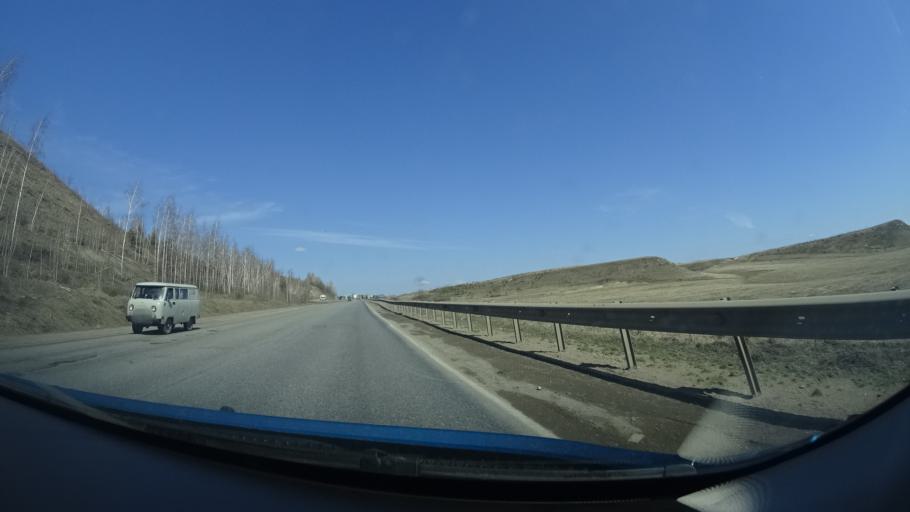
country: RU
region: Bashkortostan
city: Subkhankulovo
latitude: 54.4967
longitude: 53.9387
